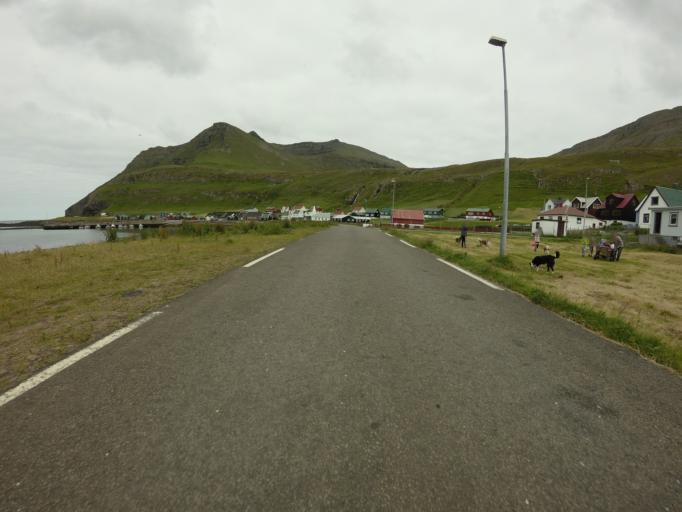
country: FO
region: Suduroy
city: Tvoroyri
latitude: 61.5236
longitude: -6.8795
